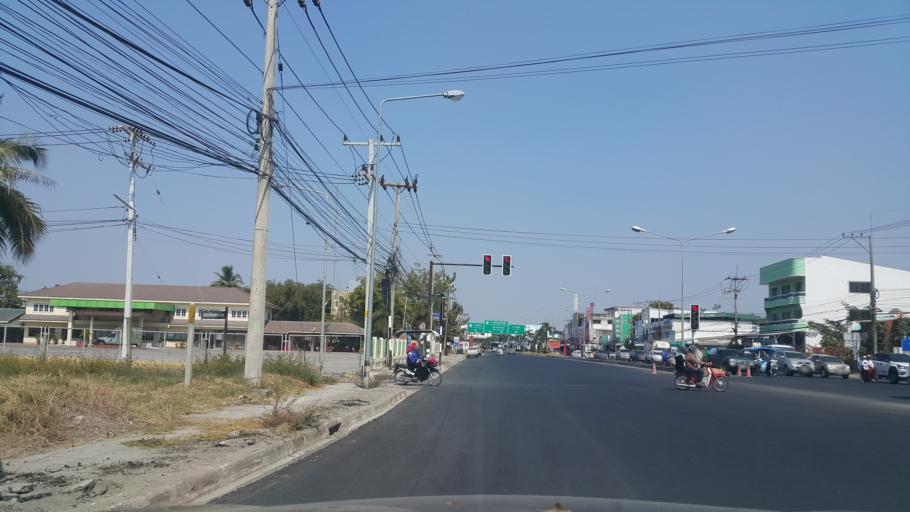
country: TH
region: Buriram
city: Satuek
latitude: 15.2918
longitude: 103.2950
